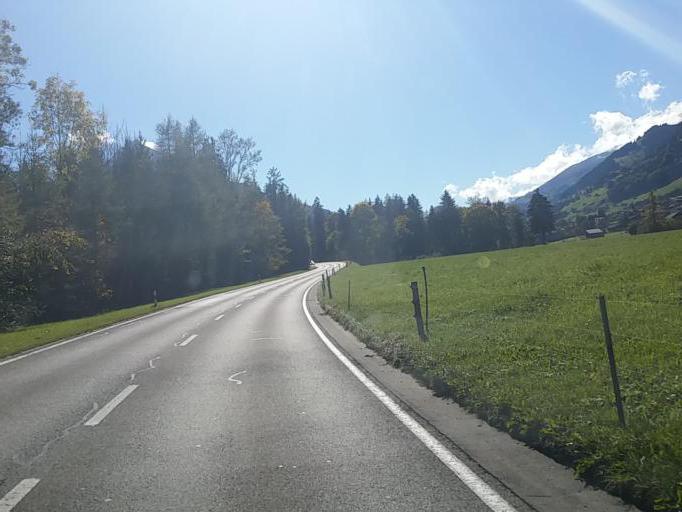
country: CH
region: Bern
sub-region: Frutigen-Niedersimmental District
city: Frutigen
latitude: 46.5992
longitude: 7.6605
